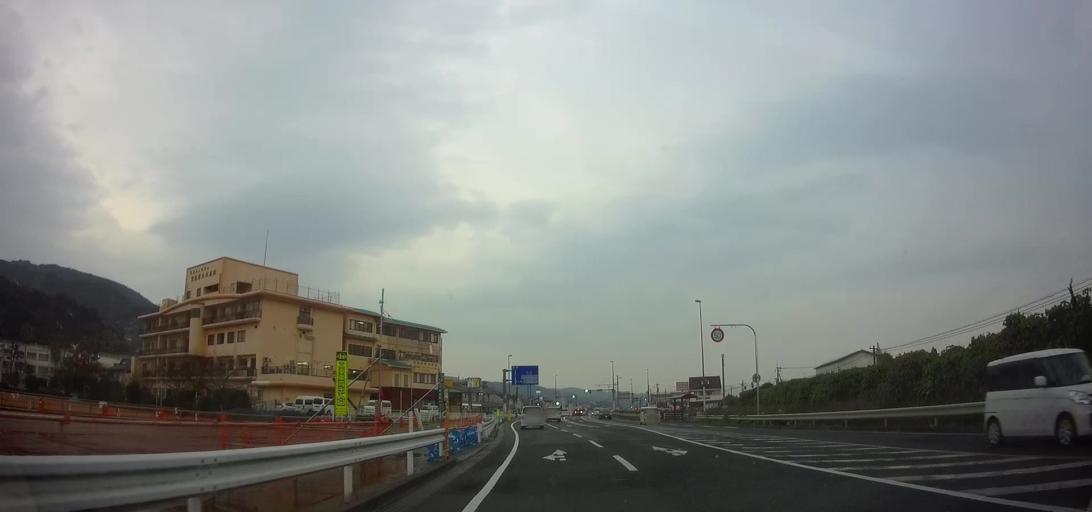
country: JP
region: Nagasaki
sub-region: Isahaya-shi
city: Isahaya
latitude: 32.8368
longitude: 130.0954
